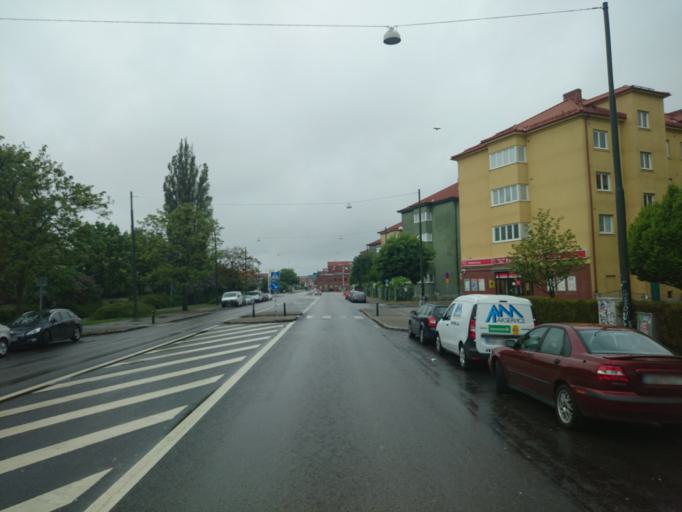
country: SE
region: Skane
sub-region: Malmo
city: Malmoe
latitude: 55.5833
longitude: 13.0217
